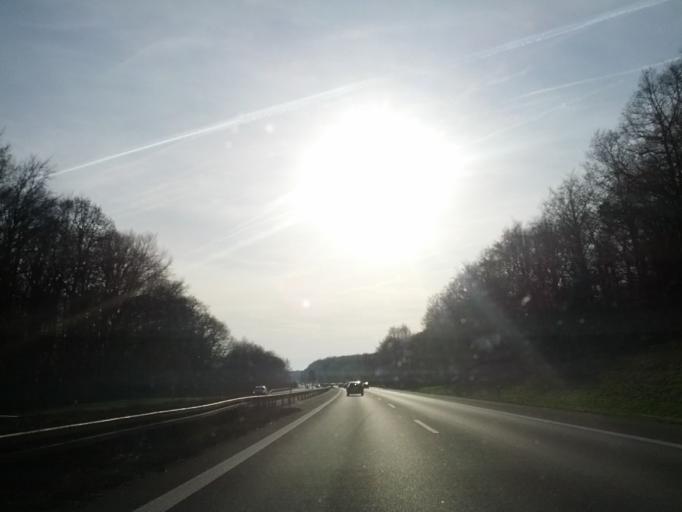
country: DE
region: Bavaria
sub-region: Regierungsbezirk Unterfranken
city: Unterpleichfeld
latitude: 49.9155
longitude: 9.9970
